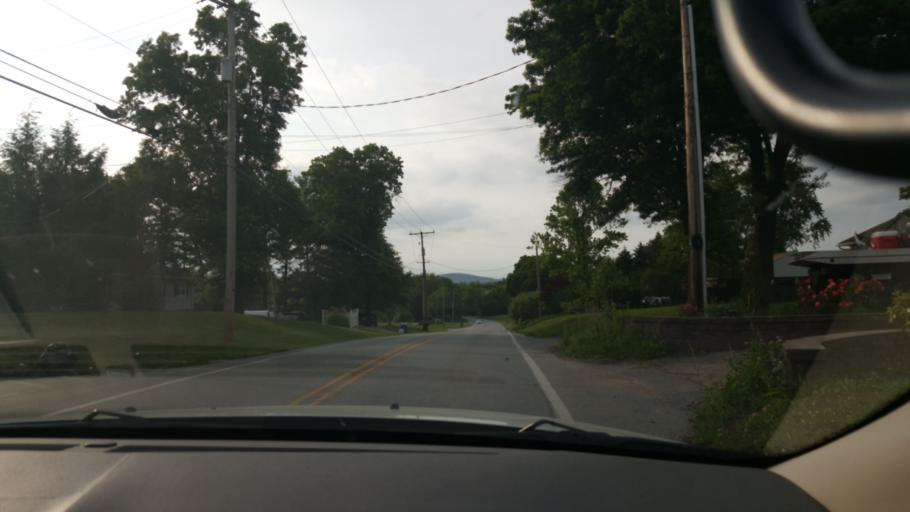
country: US
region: Pennsylvania
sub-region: York County
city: Shiloh
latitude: 39.9973
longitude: -76.7958
